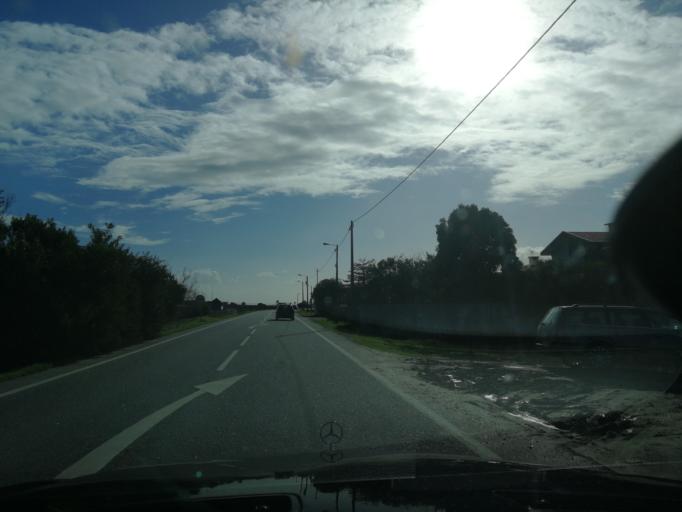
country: PT
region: Aveiro
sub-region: Estarreja
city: Pardilho
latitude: 40.7933
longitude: -8.6741
